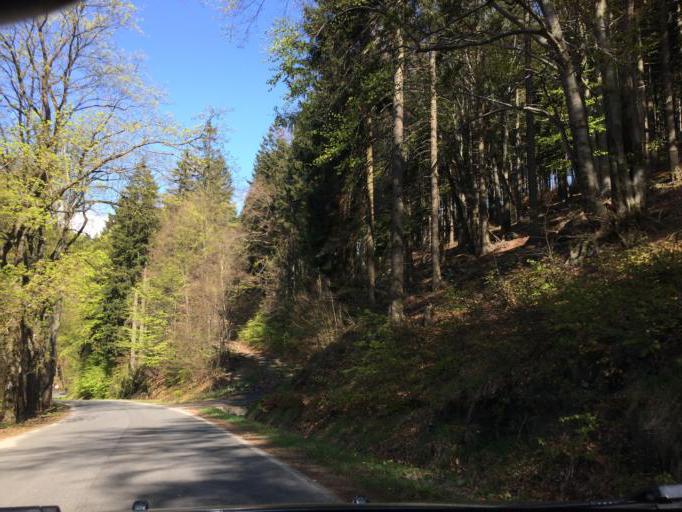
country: PL
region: Lower Silesian Voivodeship
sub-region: Powiat klodzki
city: Jugow
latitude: 50.6533
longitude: 16.5175
